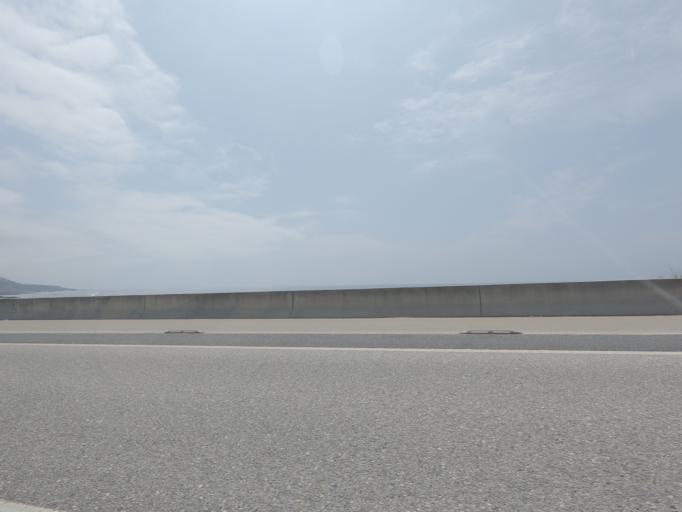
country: ES
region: Galicia
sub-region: Provincia de Pontevedra
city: Baiona
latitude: 42.1021
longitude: -8.8966
